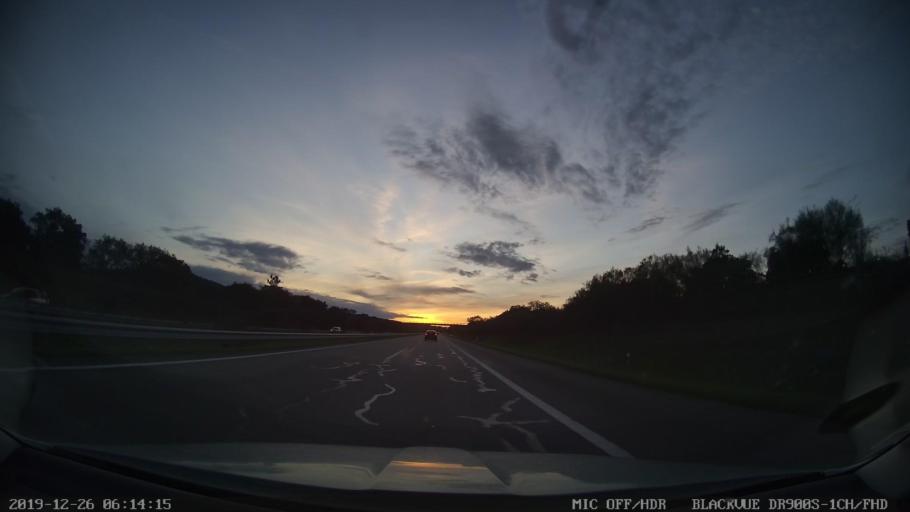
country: PT
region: Evora
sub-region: Montemor-O-Novo
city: Montemor-o-Novo
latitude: 38.6409
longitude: -8.2774
